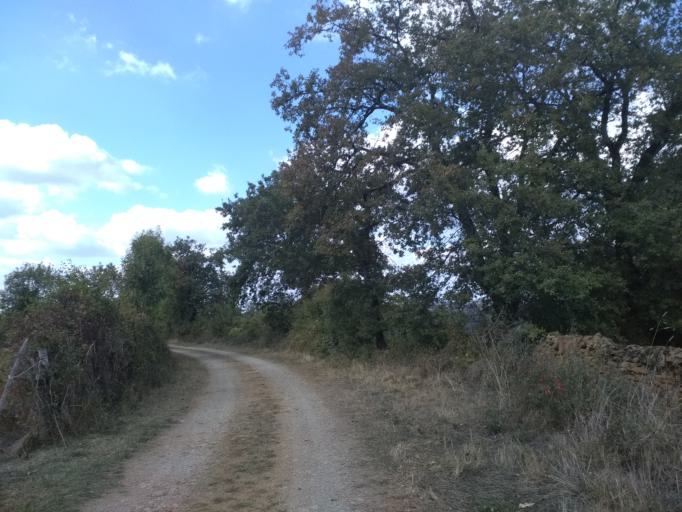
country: FR
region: Midi-Pyrenees
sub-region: Departement de l'Aveyron
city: Bozouls
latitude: 44.4758
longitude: 2.6724
